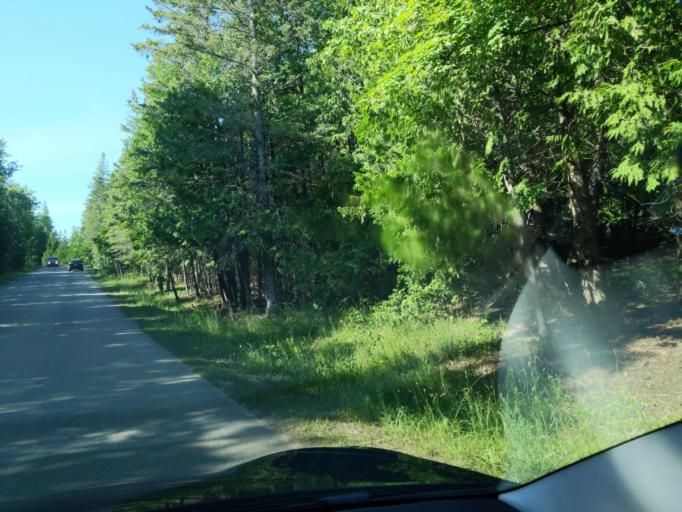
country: US
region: Michigan
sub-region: Mackinac County
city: Saint Ignace
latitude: 45.8512
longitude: -84.7184
